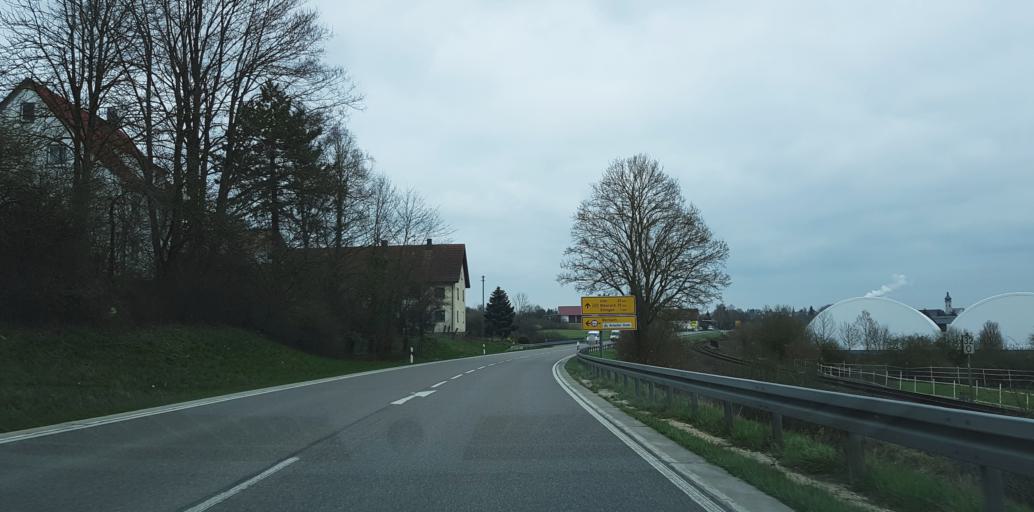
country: DE
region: Baden-Wuerttemberg
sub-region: Tuebingen Region
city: Ehingen
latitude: 48.2977
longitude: 9.7318
